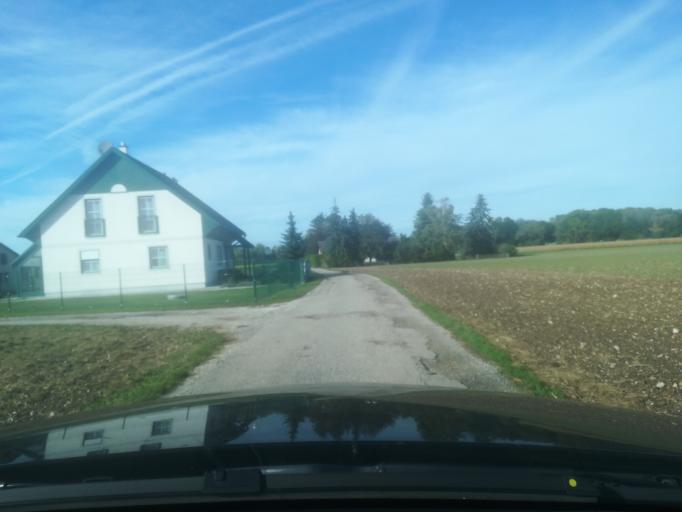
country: AT
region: Upper Austria
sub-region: Wels-Land
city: Marchtrenk
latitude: 48.2081
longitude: 14.1366
